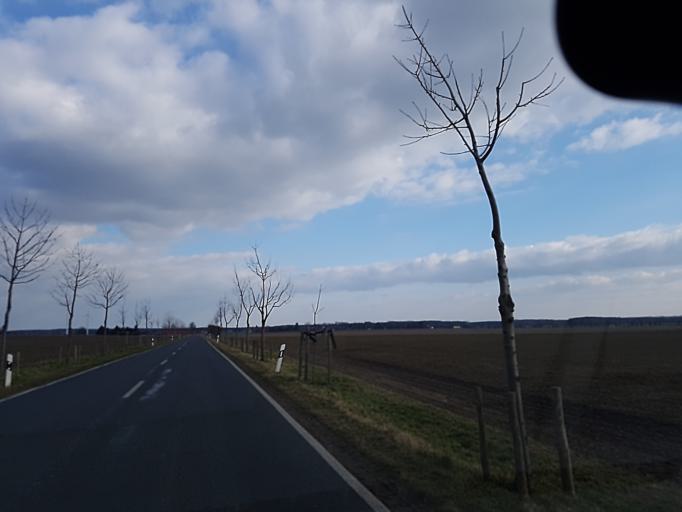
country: DE
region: Brandenburg
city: Doberlug-Kirchhain
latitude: 51.6176
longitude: 13.5710
